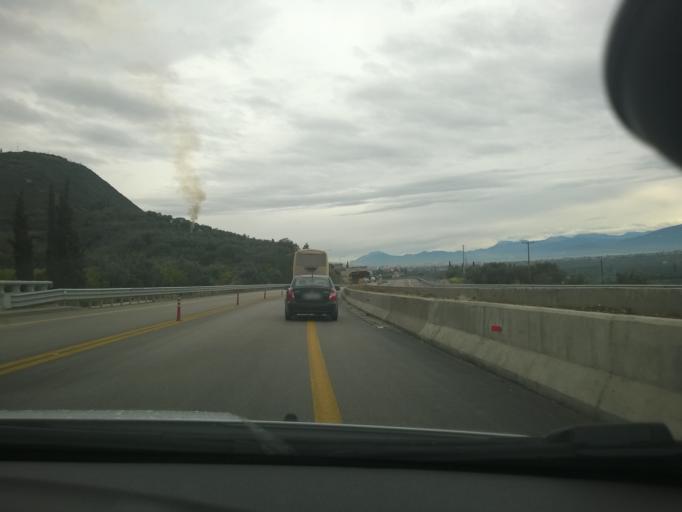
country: GR
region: West Greece
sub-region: Nomos Achaias
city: Temeni
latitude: 38.2058
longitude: 22.1391
